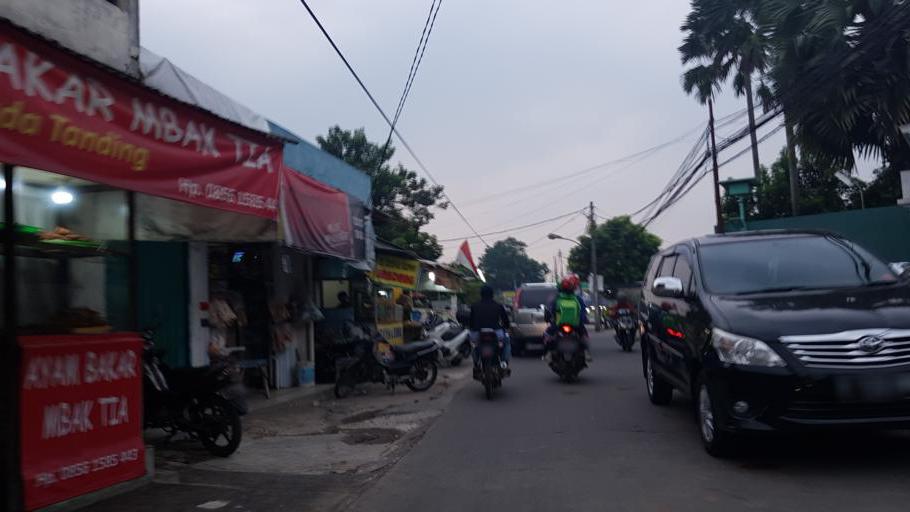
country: ID
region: West Java
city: Depok
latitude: -6.3703
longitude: 106.7997
